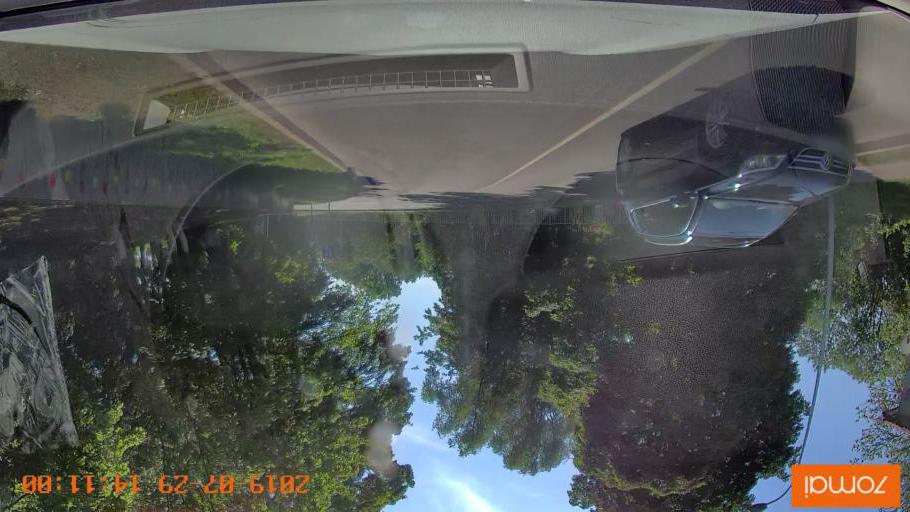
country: RU
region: Kaliningrad
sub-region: Gorod Kaliningrad
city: Baltiysk
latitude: 54.6530
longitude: 19.9106
